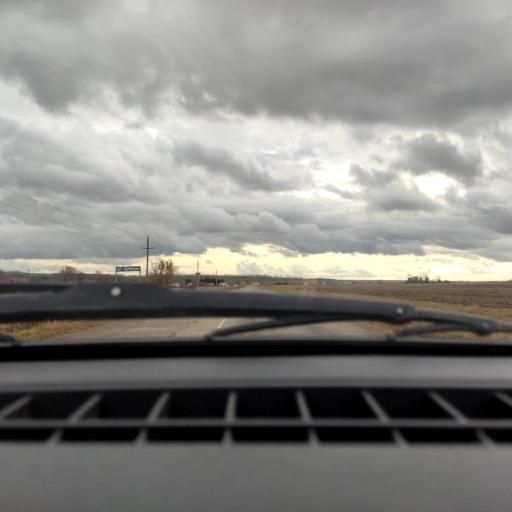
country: RU
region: Bashkortostan
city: Asanovo
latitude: 54.9334
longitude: 55.5178
